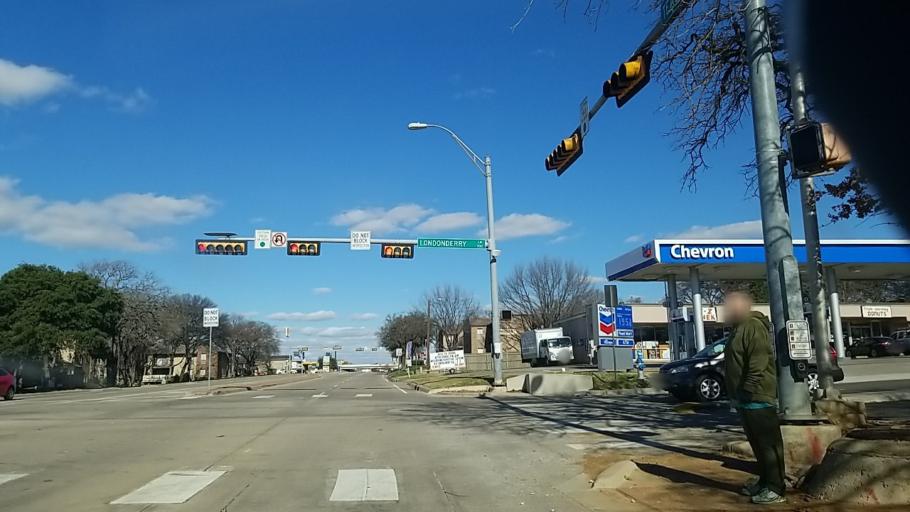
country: US
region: Texas
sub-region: Denton County
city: Denton
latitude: 33.1898
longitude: -97.1243
